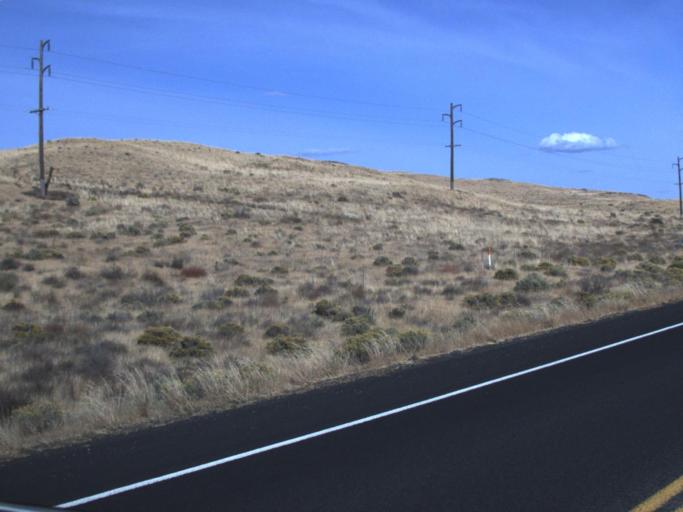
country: US
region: Oregon
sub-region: Morrow County
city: Boardman
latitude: 45.8682
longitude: -119.8162
